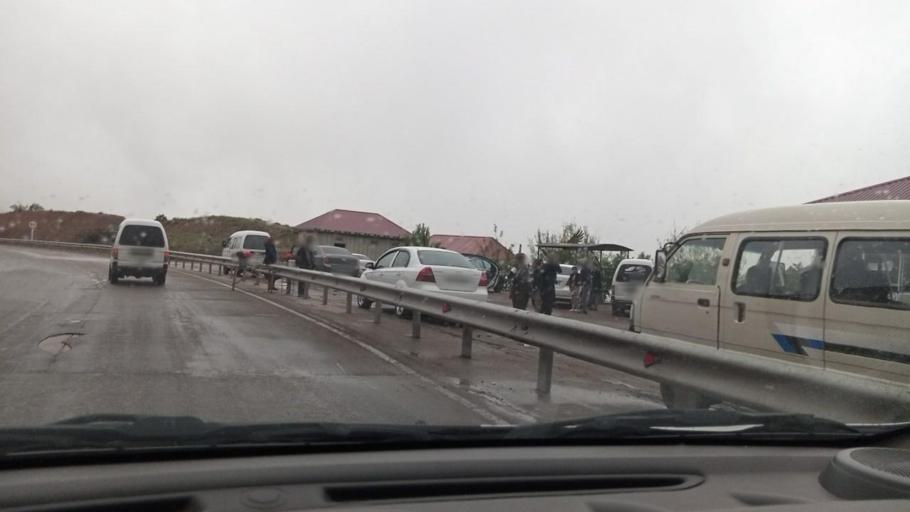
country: UZ
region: Toshkent
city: Angren
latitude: 41.1118
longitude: 70.5039
